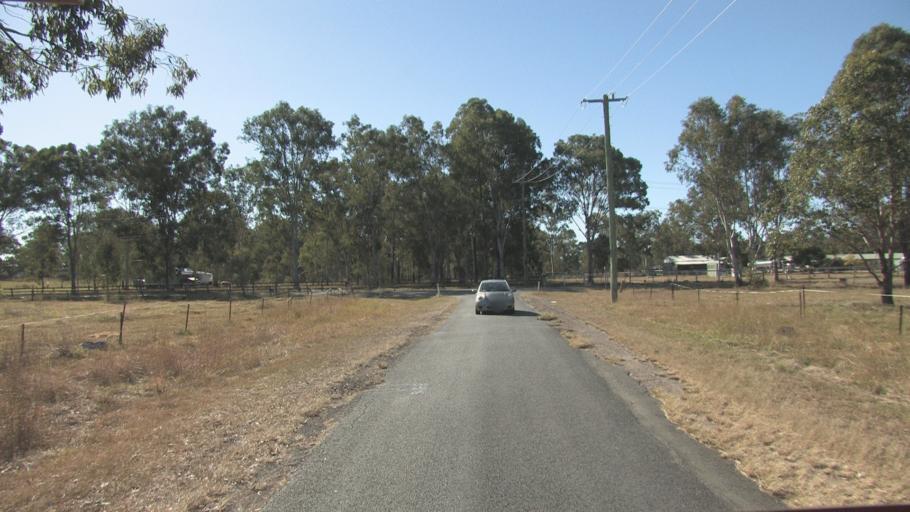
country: AU
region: Queensland
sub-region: Logan
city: North Maclean
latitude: -27.7768
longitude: 153.0197
